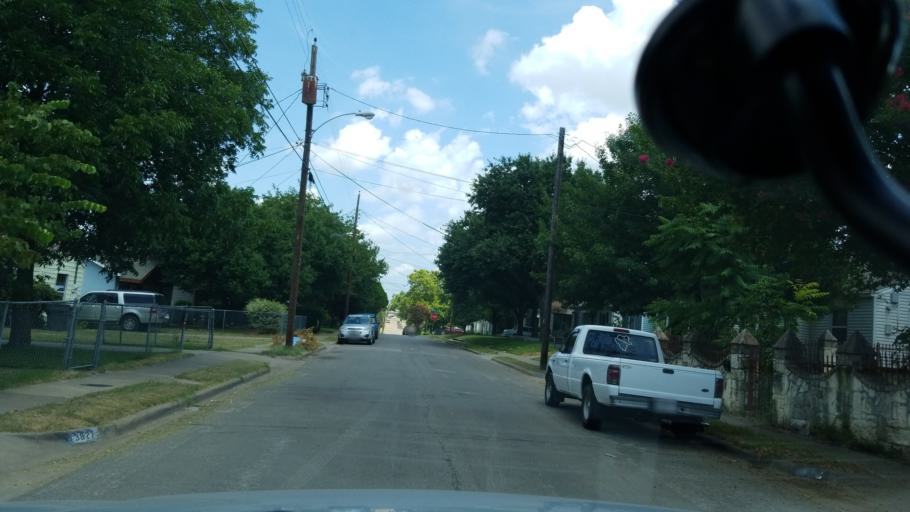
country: US
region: Texas
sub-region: Dallas County
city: Cockrell Hill
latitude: 32.7274
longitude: -96.8805
